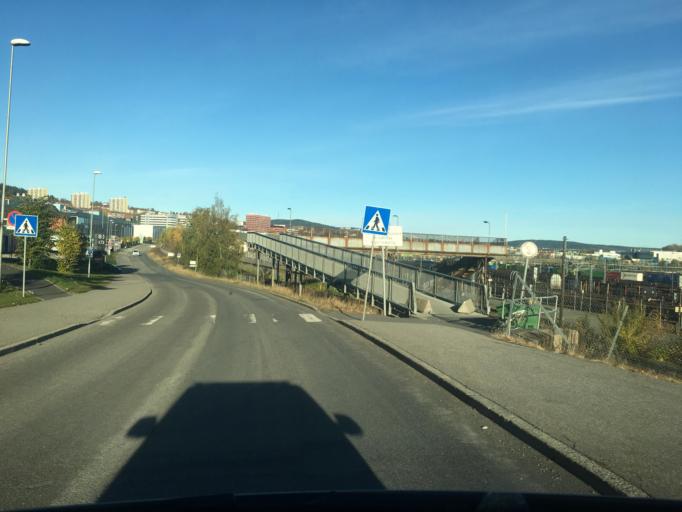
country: NO
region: Oslo
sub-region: Oslo
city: Oslo
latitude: 59.9312
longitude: 10.8337
